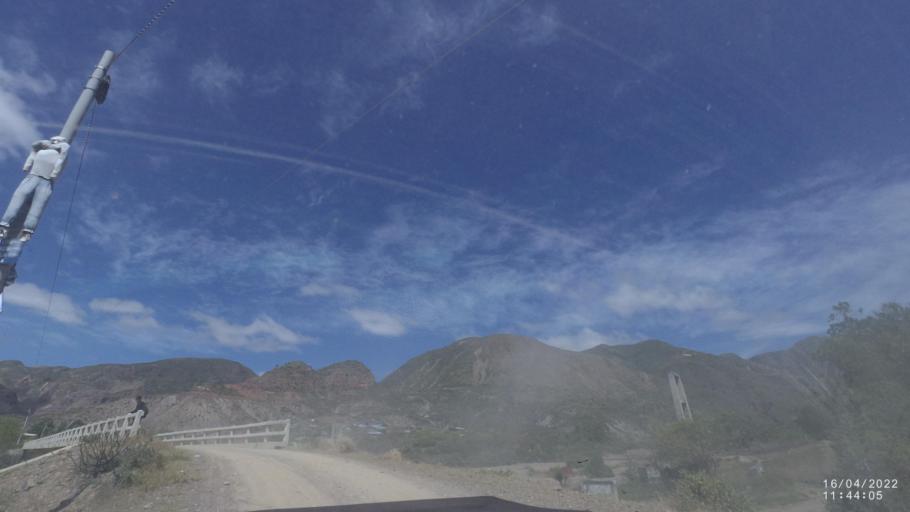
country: BO
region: Cochabamba
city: Mizque
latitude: -17.9830
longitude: -65.6316
